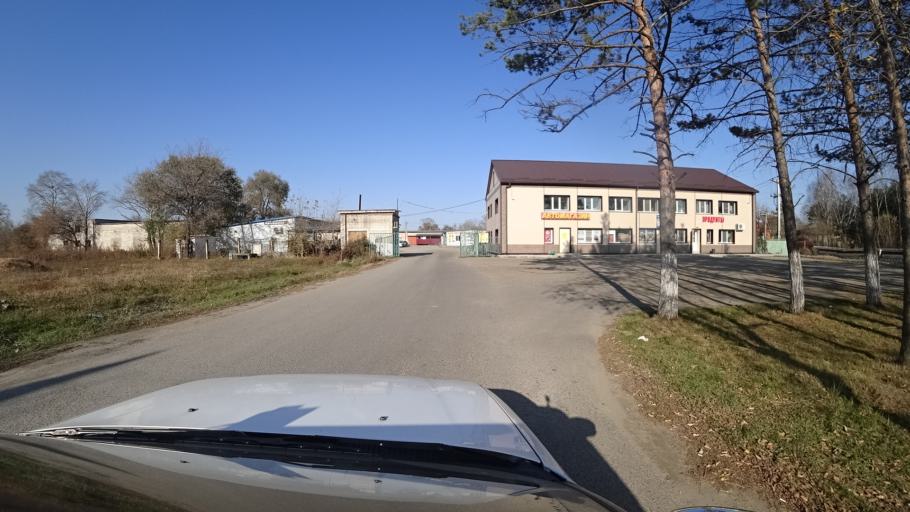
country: RU
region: Primorskiy
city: Dal'nerechensk
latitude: 45.9219
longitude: 133.7508
